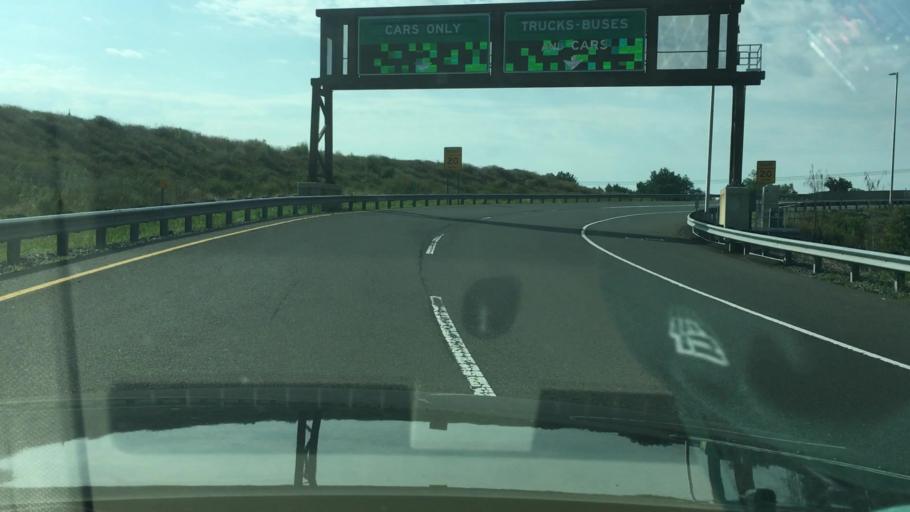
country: US
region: New Jersey
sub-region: Mercer County
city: Robbinsville
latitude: 40.1930
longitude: -74.6049
